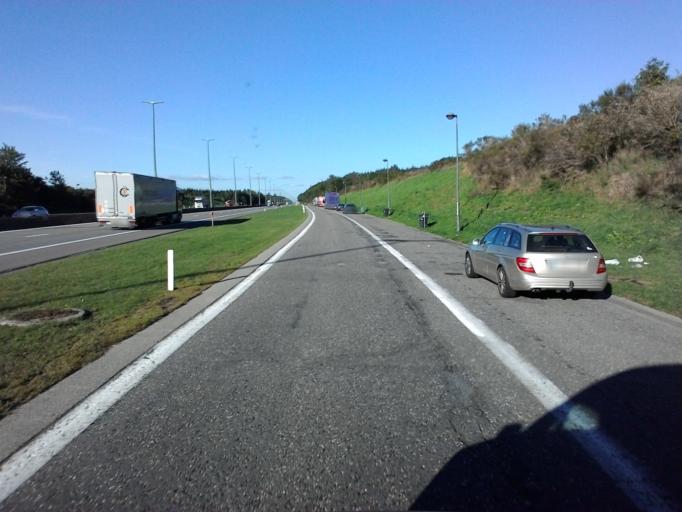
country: BE
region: Wallonia
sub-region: Province du Luxembourg
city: Bastogne
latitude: 50.0415
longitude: 5.7084
